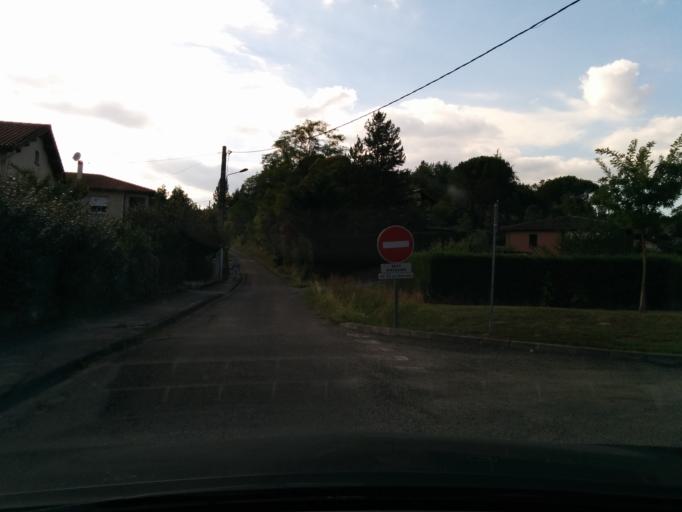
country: FR
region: Midi-Pyrenees
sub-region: Departement du Tarn-et-Garonne
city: Moissac
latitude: 44.1091
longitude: 1.0808
